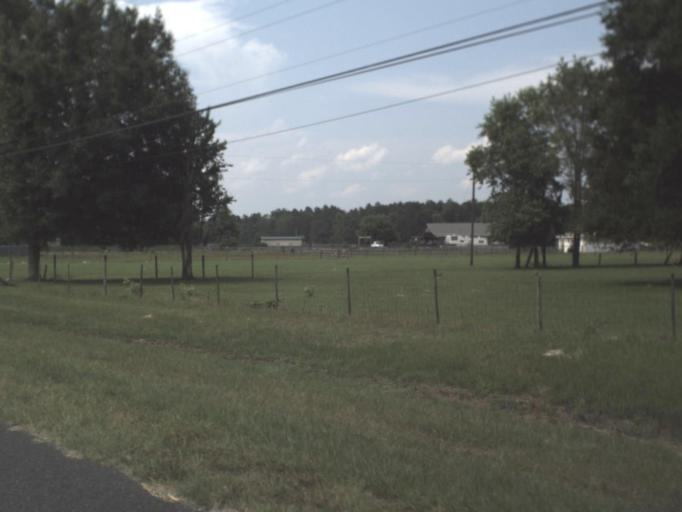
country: US
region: Florida
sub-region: Clay County
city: Green Cove Springs
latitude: 29.8855
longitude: -81.6666
